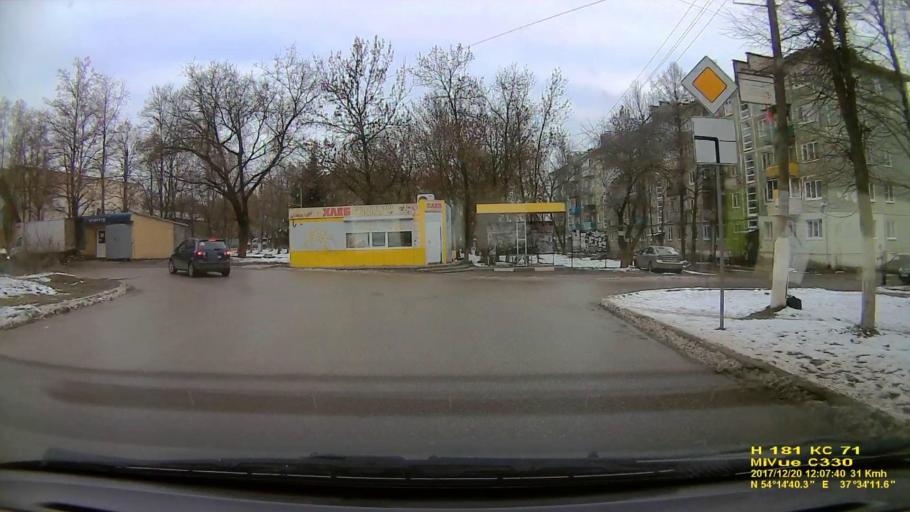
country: RU
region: Tula
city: Gorelki
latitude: 54.2445
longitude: 37.5700
